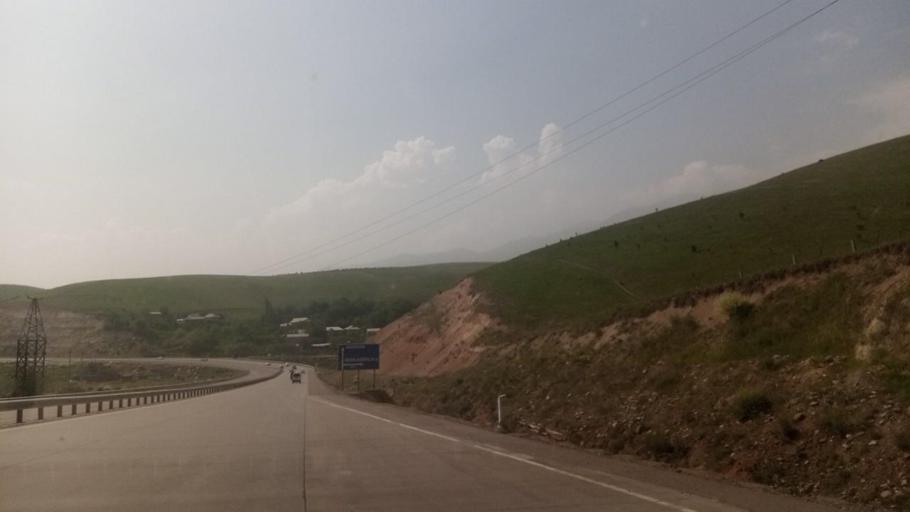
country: UZ
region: Toshkent
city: Angren
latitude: 41.0668
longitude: 70.2260
